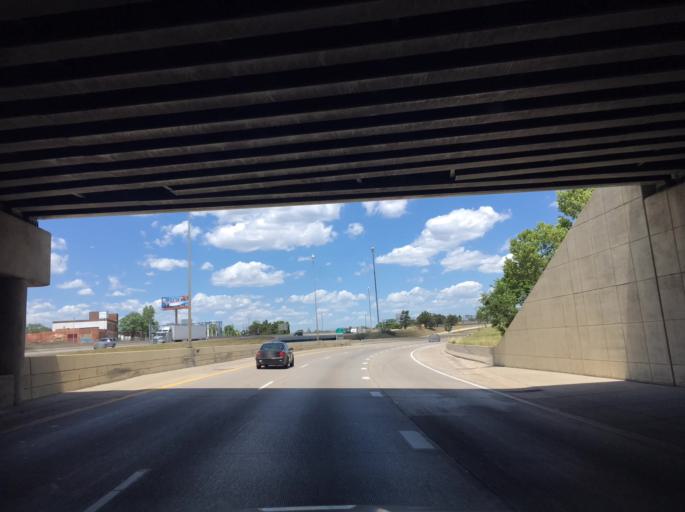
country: US
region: Michigan
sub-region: Wayne County
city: Detroit
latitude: 42.3282
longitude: -83.0857
